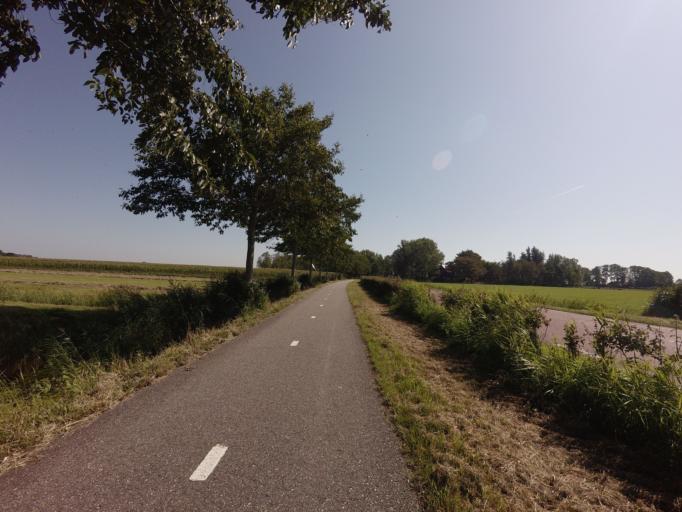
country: NL
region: Friesland
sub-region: Gemeente Dongeradeel
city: Ternaard
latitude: 53.3632
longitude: 5.9767
